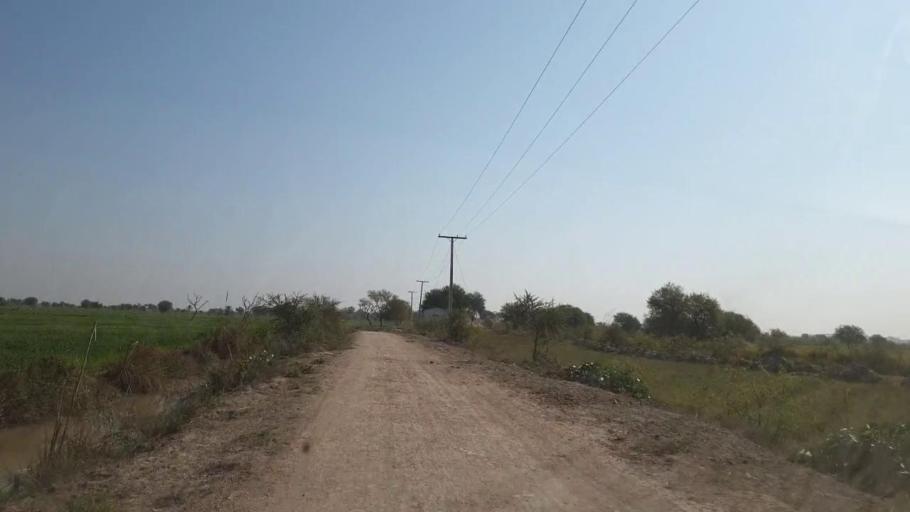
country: PK
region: Sindh
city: Mirpur Khas
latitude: 25.5325
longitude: 69.0571
